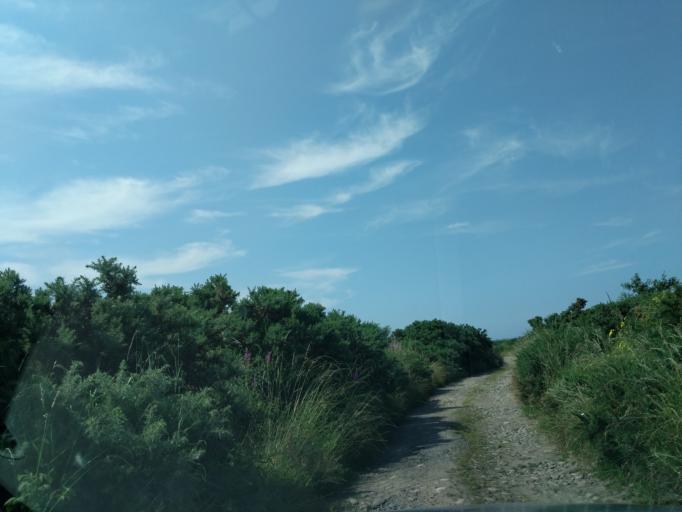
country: GB
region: Scotland
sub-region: Moray
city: Lossiemouth
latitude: 57.7181
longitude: -3.3263
